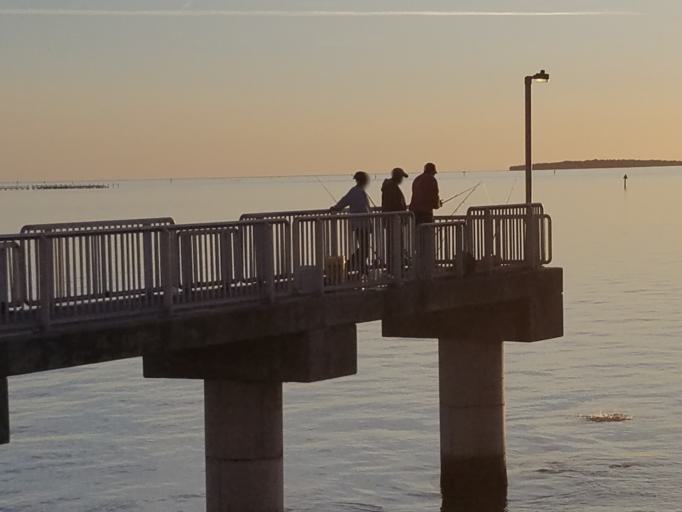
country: US
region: Florida
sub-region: Levy County
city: Inglis
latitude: 29.1338
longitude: -83.0333
